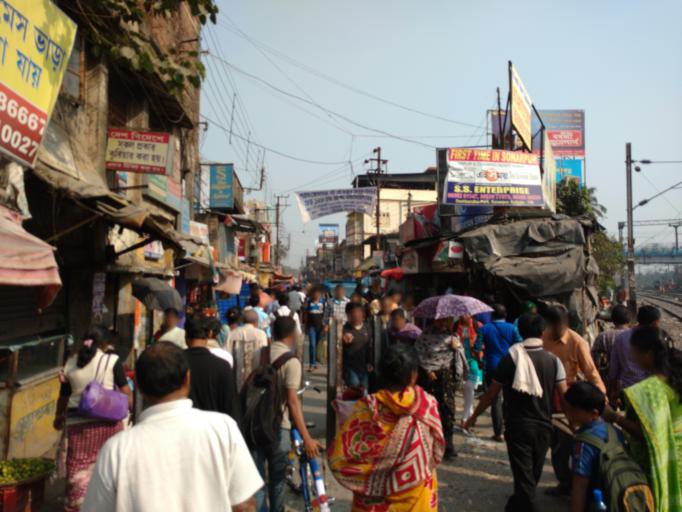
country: IN
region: West Bengal
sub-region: South 24 Paraganas
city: Champahati
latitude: 22.4423
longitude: 88.4317
